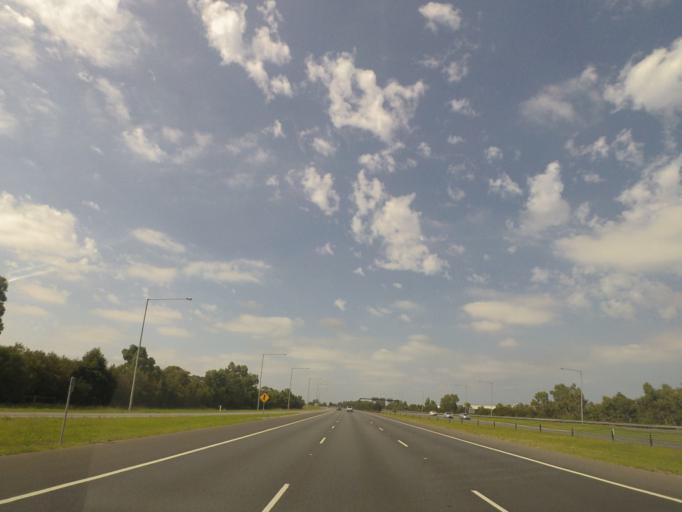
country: AU
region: Victoria
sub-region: Greater Dandenong
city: Keysborough
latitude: -38.0140
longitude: 145.1880
